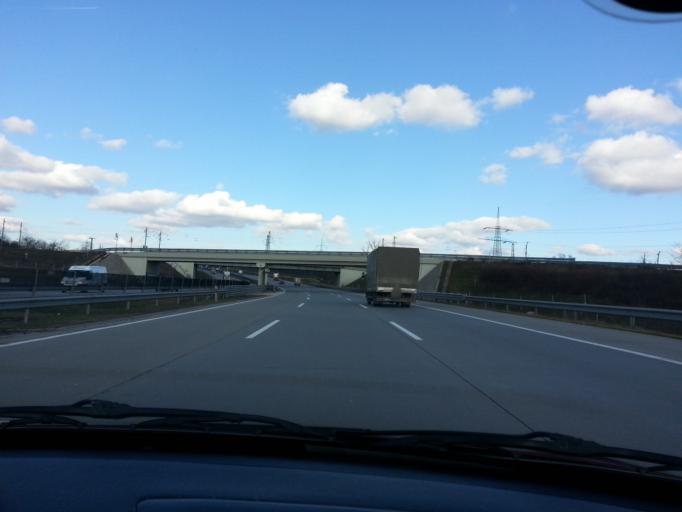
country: HU
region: Pest
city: Ecser
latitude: 47.4399
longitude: 19.3320
